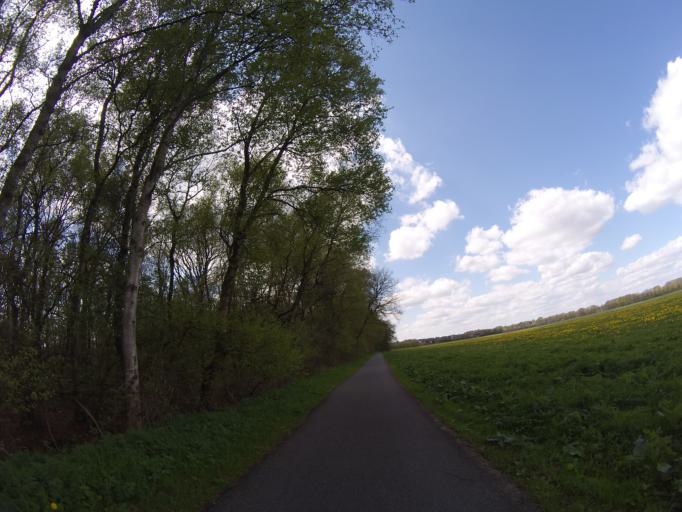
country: NL
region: Drenthe
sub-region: Gemeente Coevorden
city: Dalen
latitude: 52.7595
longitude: 6.7361
